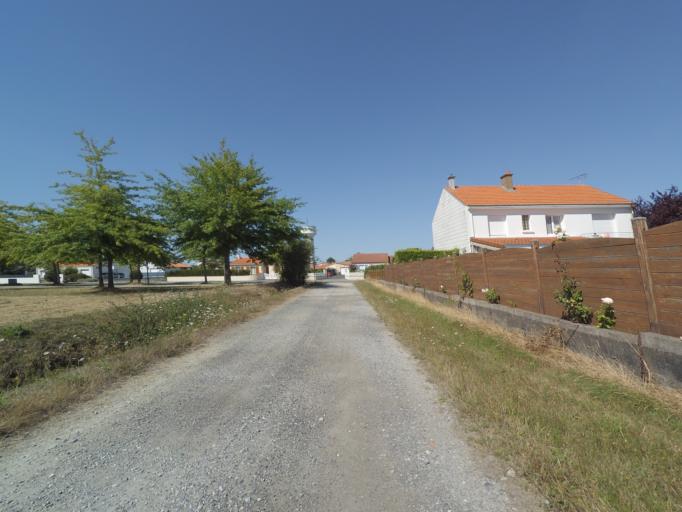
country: FR
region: Pays de la Loire
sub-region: Departement de la Loire-Atlantique
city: Vieillevigne
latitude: 46.9710
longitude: -1.4375
